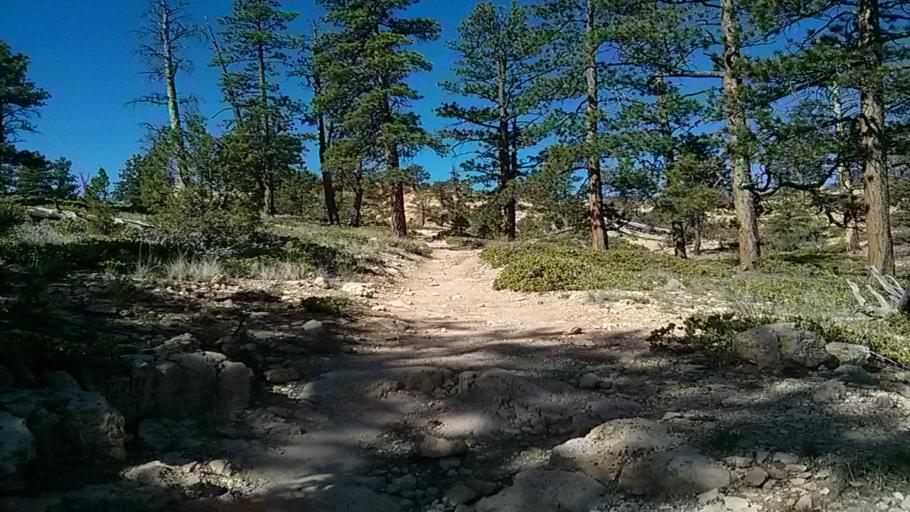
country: US
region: Utah
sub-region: Garfield County
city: Panguitch
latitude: 37.6365
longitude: -112.1328
